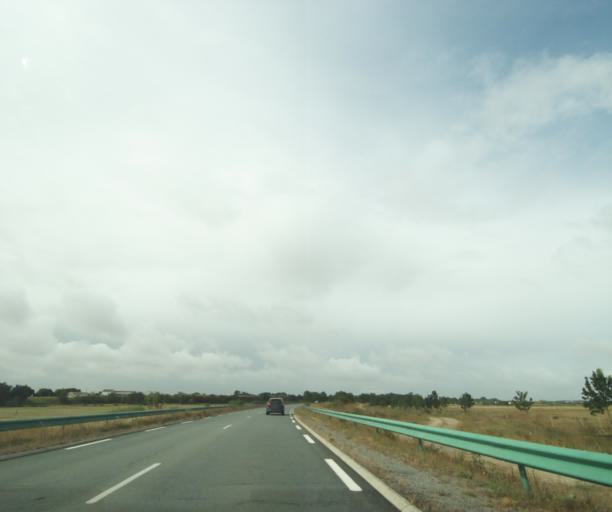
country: FR
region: Poitou-Charentes
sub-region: Departement de la Charente-Maritime
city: Andilly
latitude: 46.2475
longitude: -1.0696
